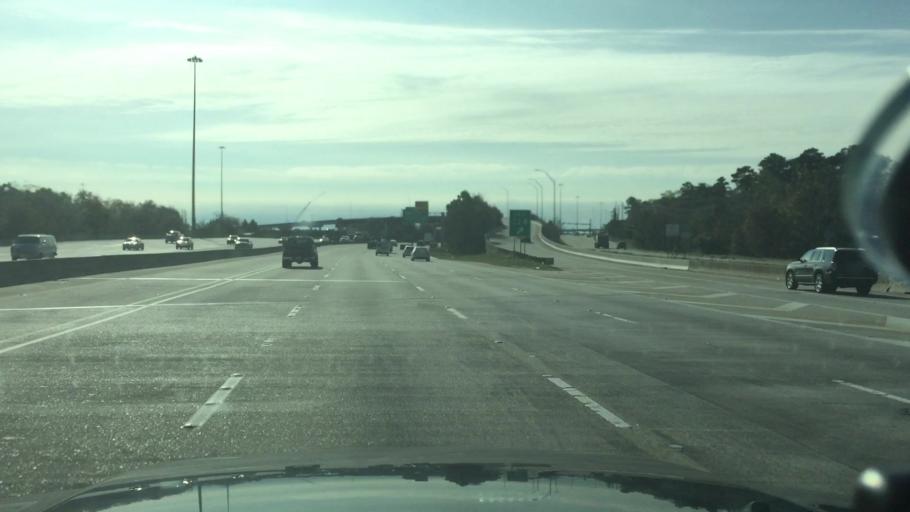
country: US
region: Texas
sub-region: Harris County
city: Spring
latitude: 30.1101
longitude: -95.4365
